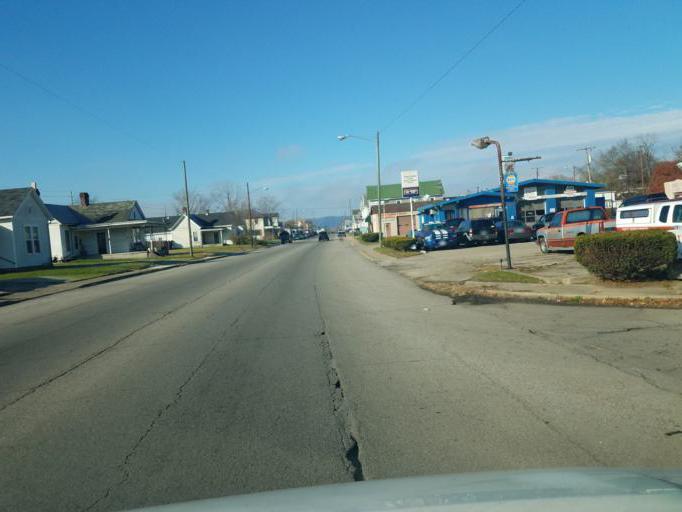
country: US
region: Ohio
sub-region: Scioto County
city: Portsmouth
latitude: 38.7398
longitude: -82.9798
